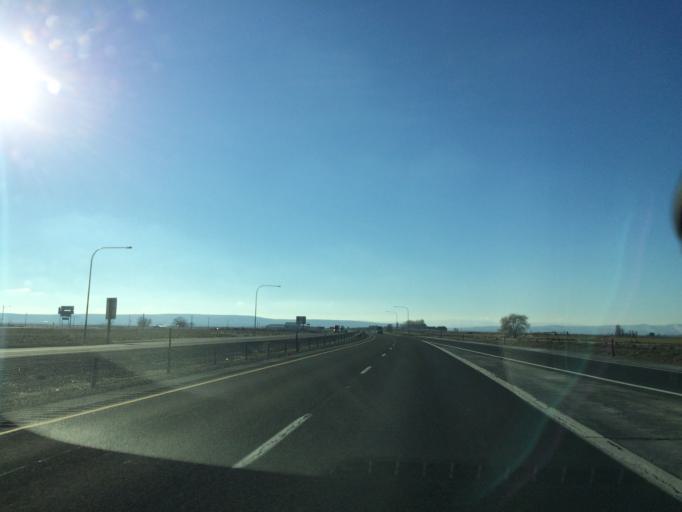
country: US
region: Washington
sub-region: Grant County
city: Quincy
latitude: 47.0838
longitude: -119.8633
